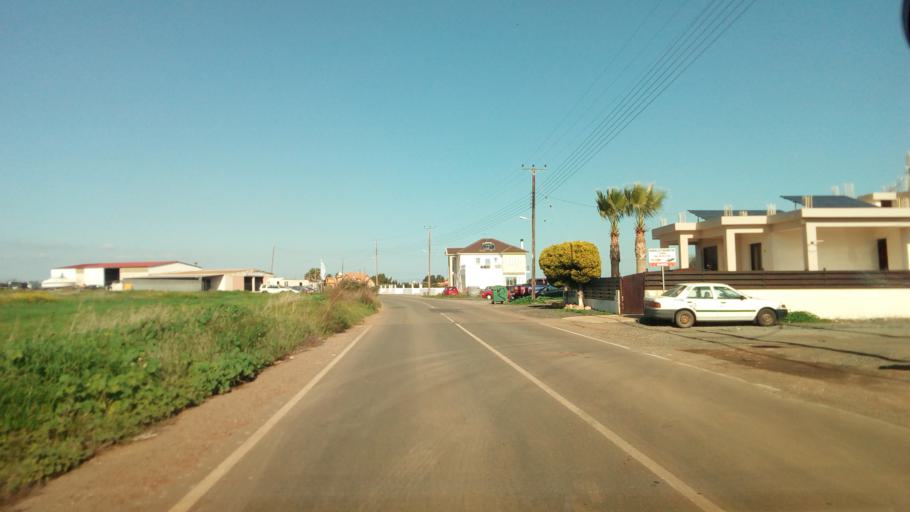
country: CY
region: Ammochostos
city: Liopetri
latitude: 34.9863
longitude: 33.8489
